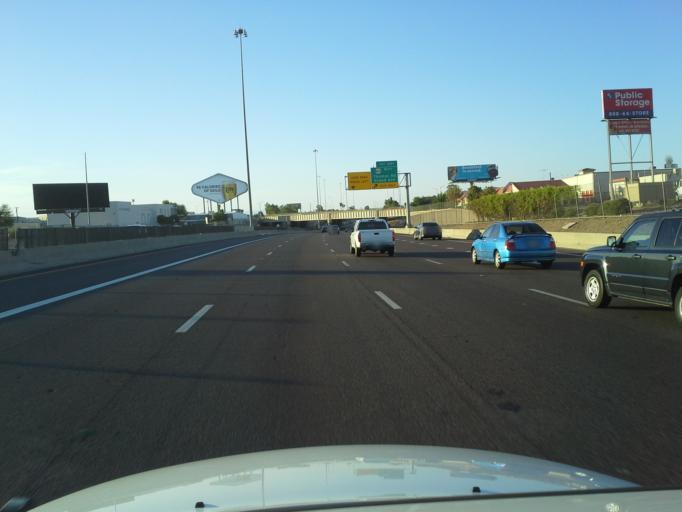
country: US
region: Arizona
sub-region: Maricopa County
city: Phoenix
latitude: 33.4737
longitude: -112.1128
